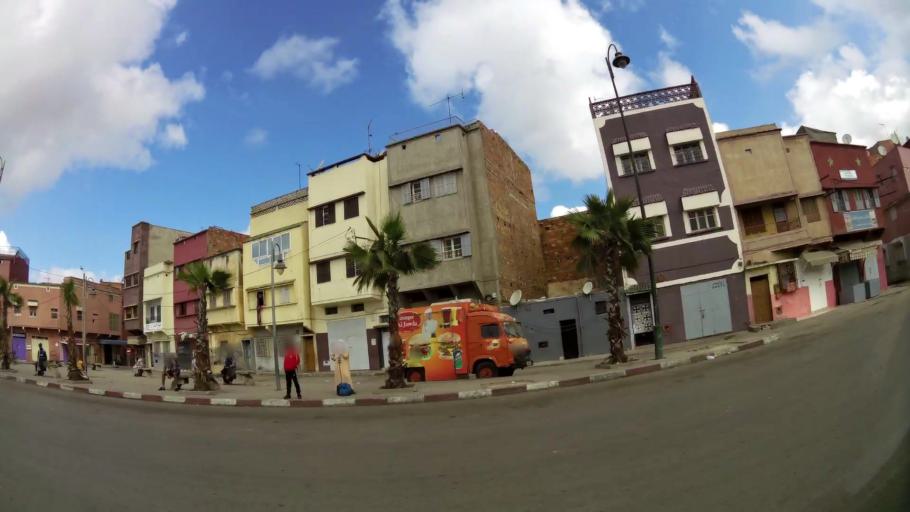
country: MA
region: Gharb-Chrarda-Beni Hssen
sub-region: Kenitra Province
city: Kenitra
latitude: 34.2618
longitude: -6.5630
